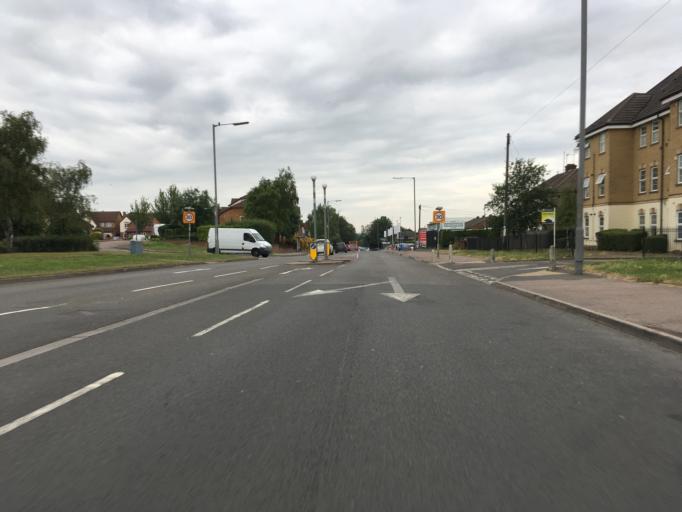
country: GB
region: England
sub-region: Central Bedfordshire
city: Dunstable
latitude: 51.8779
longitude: -0.5088
